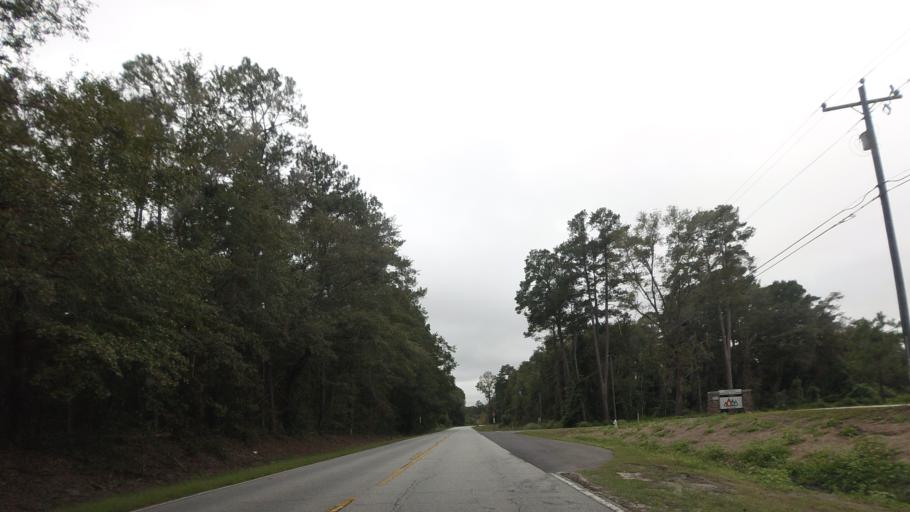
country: US
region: Georgia
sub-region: Lowndes County
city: Valdosta
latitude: 30.8681
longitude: -83.2444
